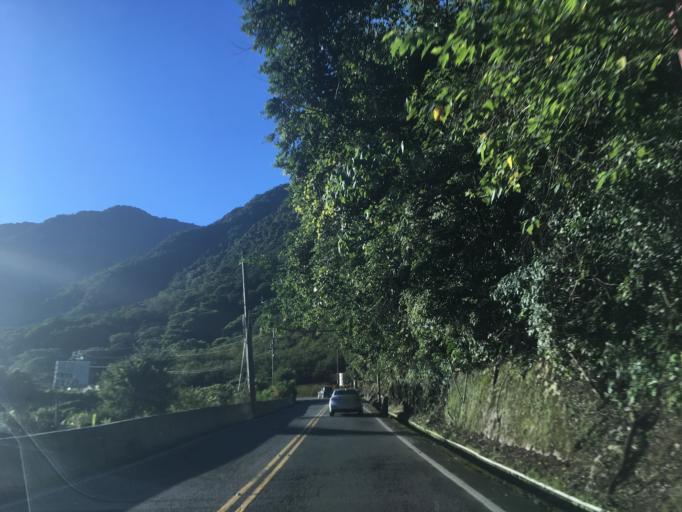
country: TW
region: Taiwan
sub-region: Nantou
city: Puli
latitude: 23.9959
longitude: 121.0705
